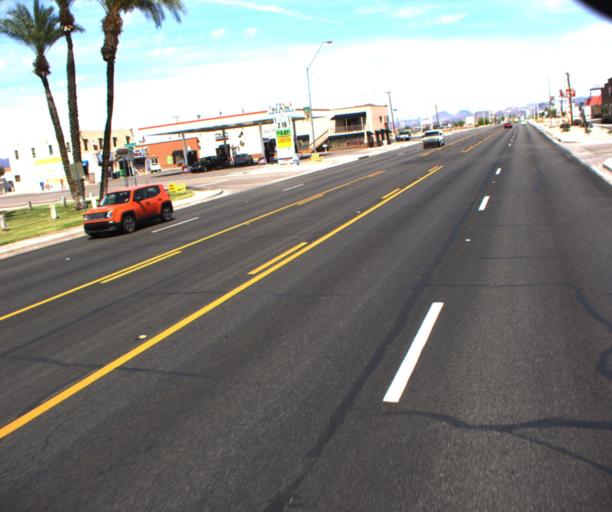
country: US
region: Arizona
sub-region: La Paz County
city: Parker
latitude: 34.1534
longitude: -114.2820
